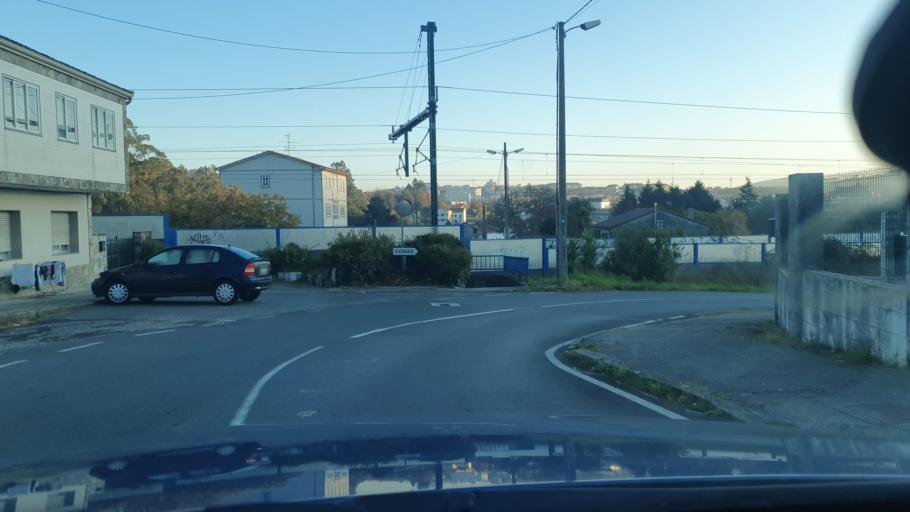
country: ES
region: Galicia
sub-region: Provincia da Coruna
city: Santiago de Compostela
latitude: 42.8592
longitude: -8.5701
